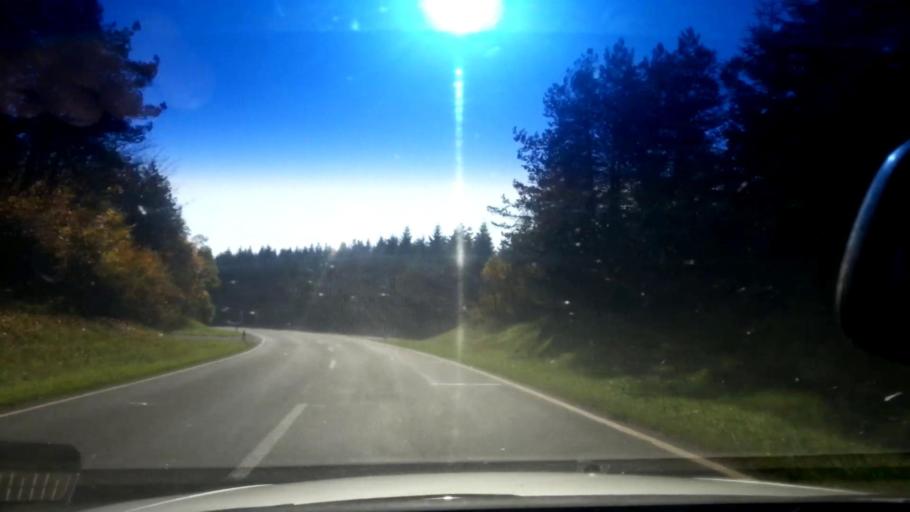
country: DE
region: Bavaria
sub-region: Upper Franconia
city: Wonsees
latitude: 49.9725
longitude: 11.2495
